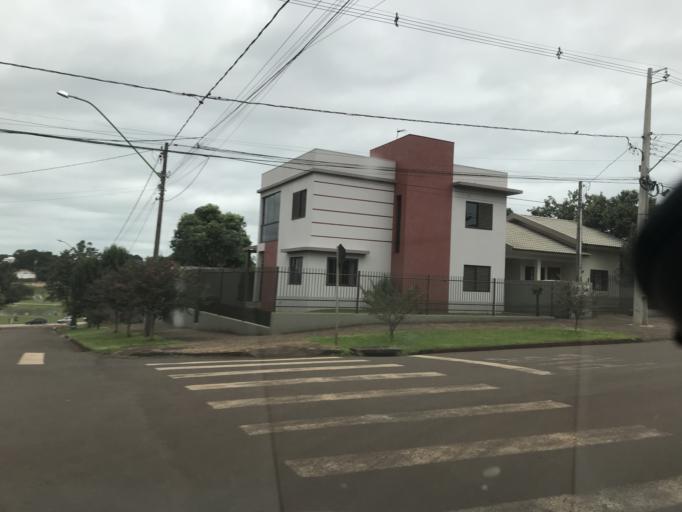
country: BR
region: Parana
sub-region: Palotina
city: Palotina
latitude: -24.2868
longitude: -53.8326
